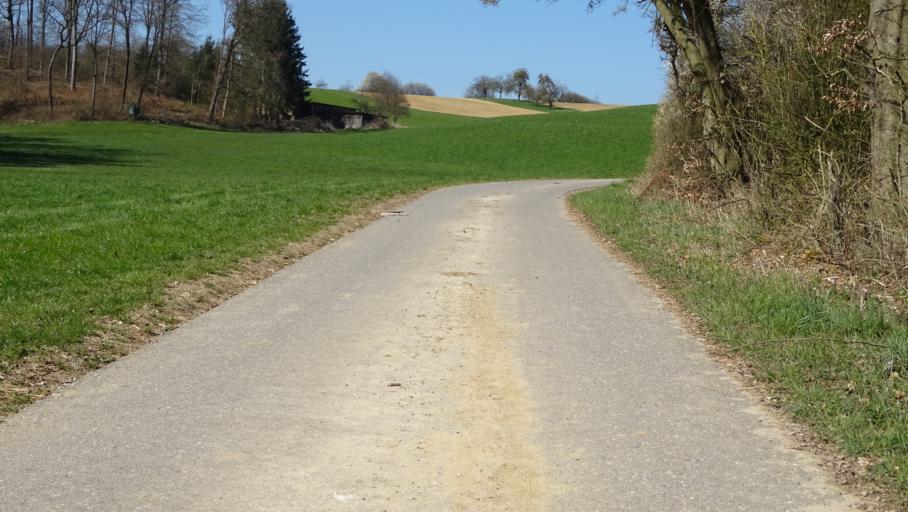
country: DE
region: Baden-Wuerttemberg
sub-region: Karlsruhe Region
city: Limbach
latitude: 49.4168
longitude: 9.2387
